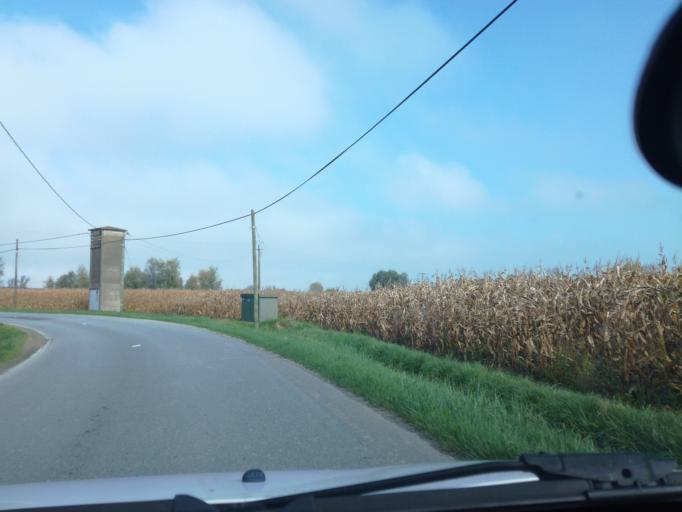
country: FR
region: Brittany
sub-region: Departement d'Ille-et-Vilaine
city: Cherrueix
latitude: 48.5926
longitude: -1.7180
